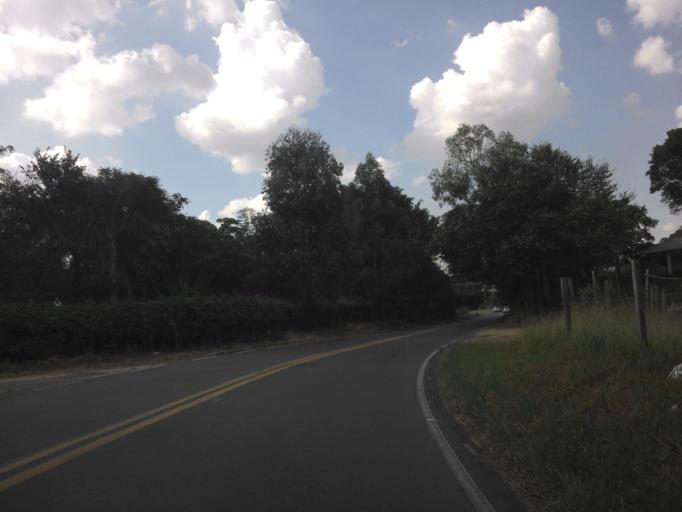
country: BR
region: Sao Paulo
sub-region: Vinhedo
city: Vinhedo
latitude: -23.0090
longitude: -47.0034
